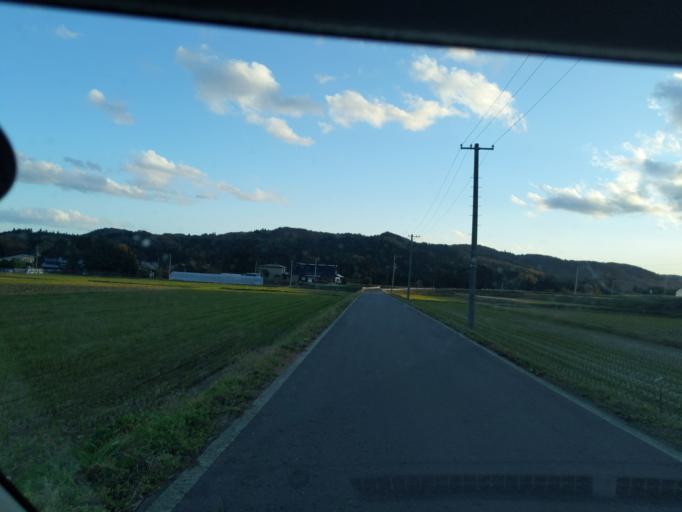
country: JP
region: Iwate
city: Mizusawa
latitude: 39.0382
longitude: 141.0556
